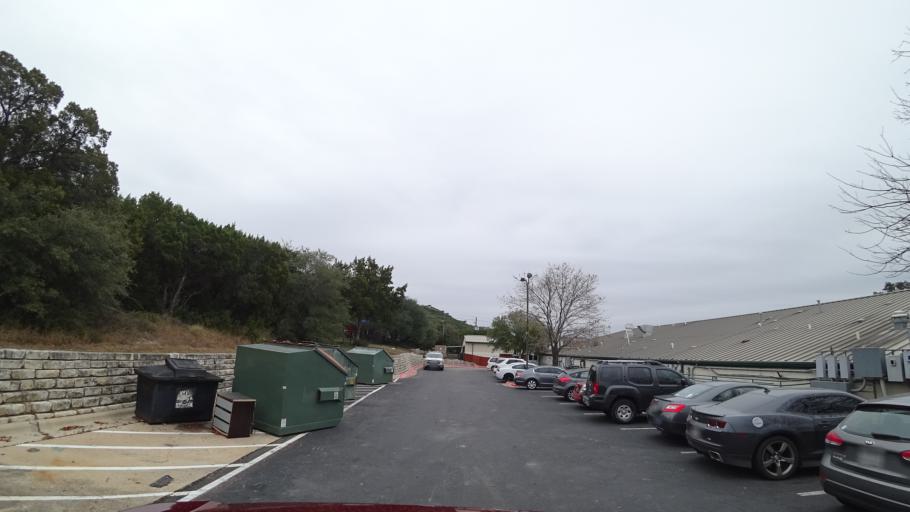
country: US
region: Texas
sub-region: Travis County
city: West Lake Hills
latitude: 30.3704
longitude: -97.7998
